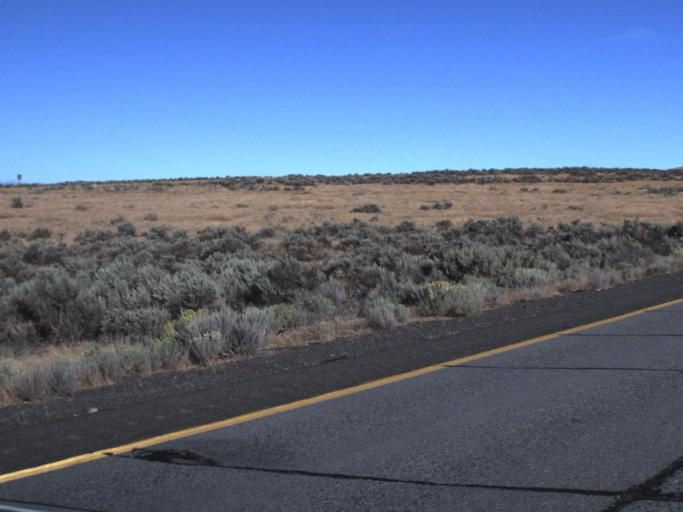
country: US
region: Washington
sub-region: Kittitas County
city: Kittitas
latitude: 46.8402
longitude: -120.3718
